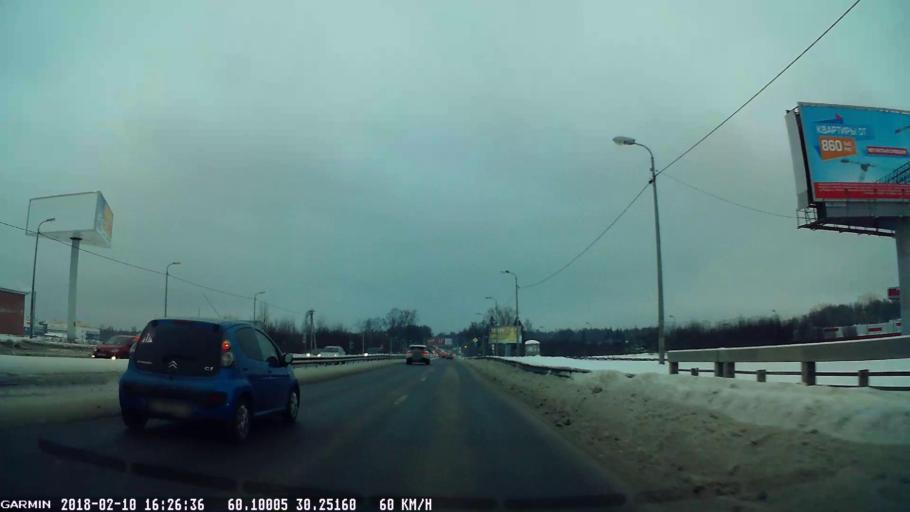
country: RU
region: St.-Petersburg
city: Pargolovo
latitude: 60.0999
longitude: 30.2518
